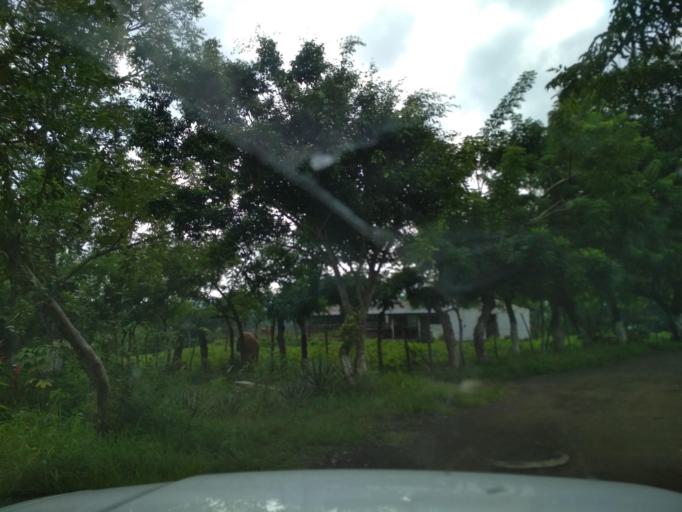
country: MX
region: Veracruz
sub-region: San Andres Tuxtla
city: Matacapan
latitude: 18.4448
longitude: -95.1778
